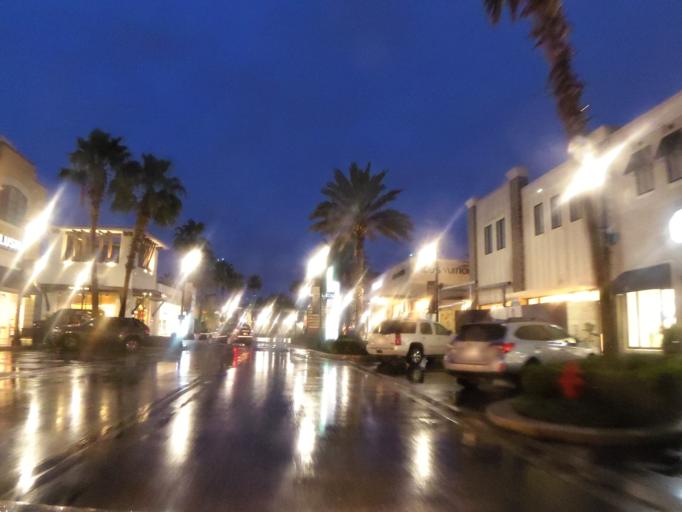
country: US
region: Florida
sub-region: Duval County
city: Jacksonville Beach
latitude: 30.2541
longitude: -81.5253
